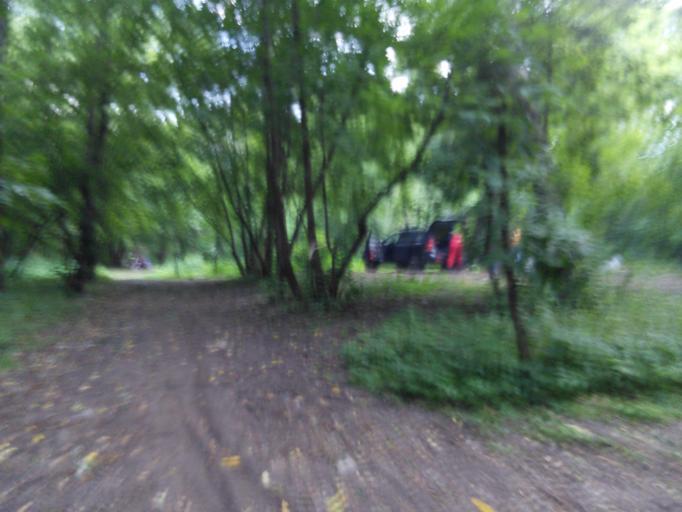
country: RU
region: Moskovskaya
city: Bogorodskoye
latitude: 55.8118
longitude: 37.6959
